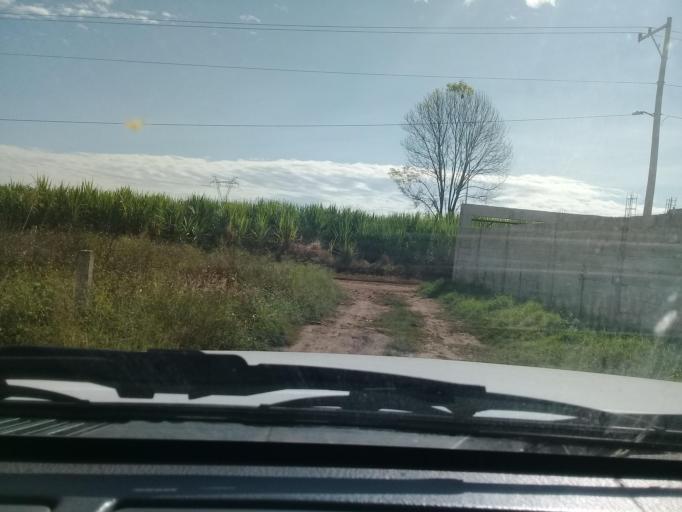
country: MX
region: Veracruz
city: El Castillo
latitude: 19.5459
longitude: -96.8785
